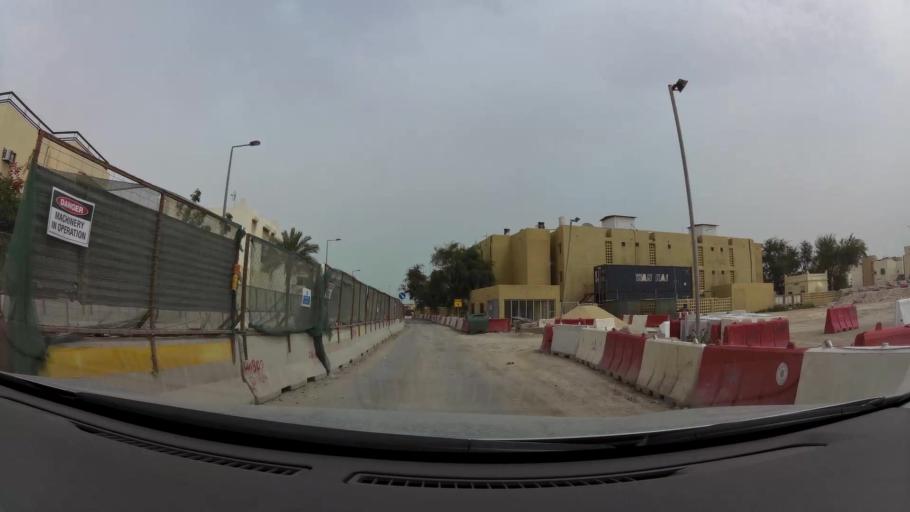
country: QA
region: Baladiyat ad Dawhah
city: Doha
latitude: 25.2438
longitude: 51.5631
